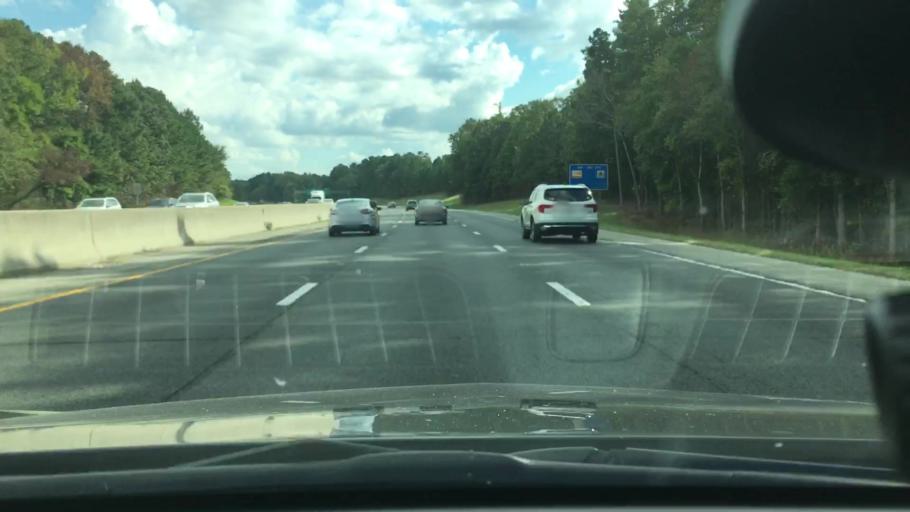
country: US
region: North Carolina
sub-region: Orange County
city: Chapel Hill
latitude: 35.9205
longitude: -78.9857
